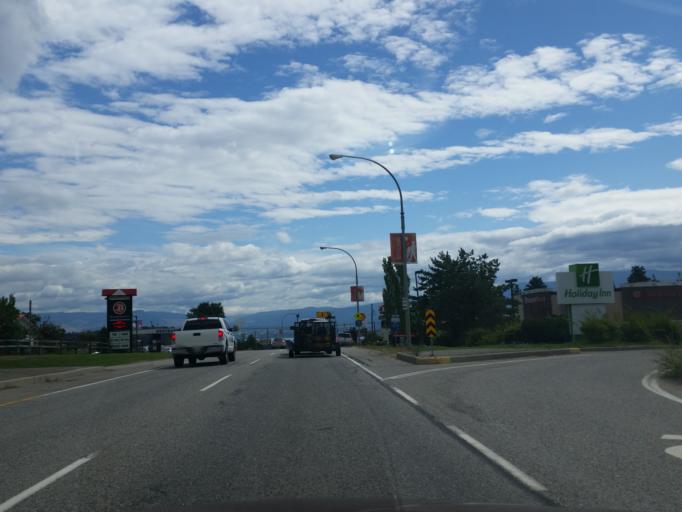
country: CA
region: British Columbia
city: West Kelowna
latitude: 49.8284
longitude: -119.6369
